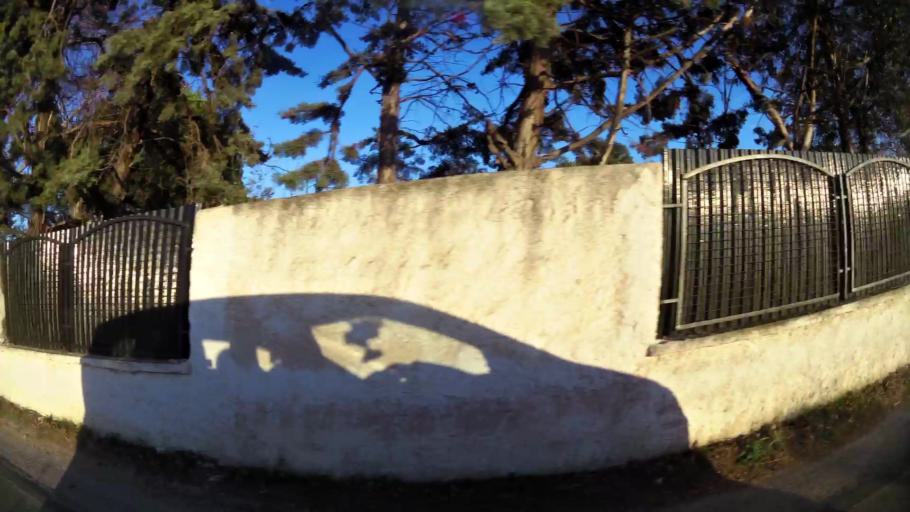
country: GR
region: Attica
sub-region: Nomarchia Anatolikis Attikis
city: Rafina
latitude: 38.0060
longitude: 24.0088
